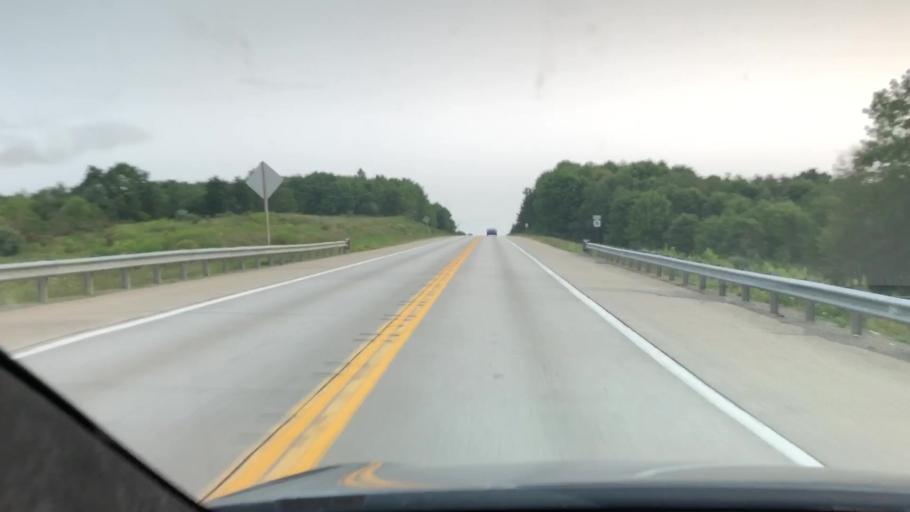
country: US
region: Pennsylvania
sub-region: Mercer County
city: Grove City
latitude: 41.2308
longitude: -79.9551
